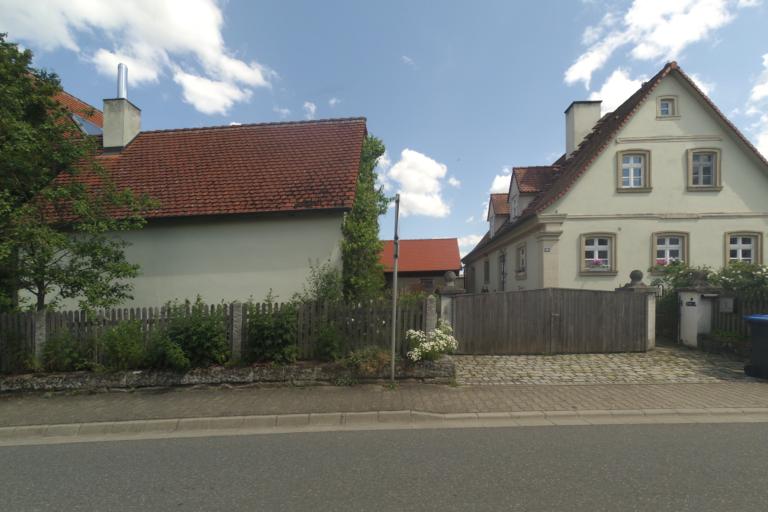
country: DE
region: Bavaria
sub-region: Upper Franconia
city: Hallerndorf
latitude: 49.7422
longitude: 10.9624
